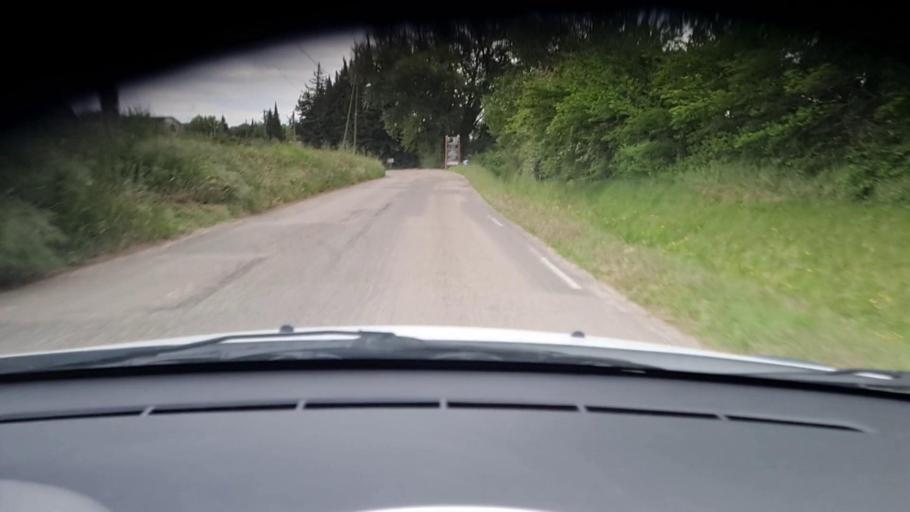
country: FR
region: Languedoc-Roussillon
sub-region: Departement du Gard
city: Castillon-du-Gard
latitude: 43.9667
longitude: 4.5154
